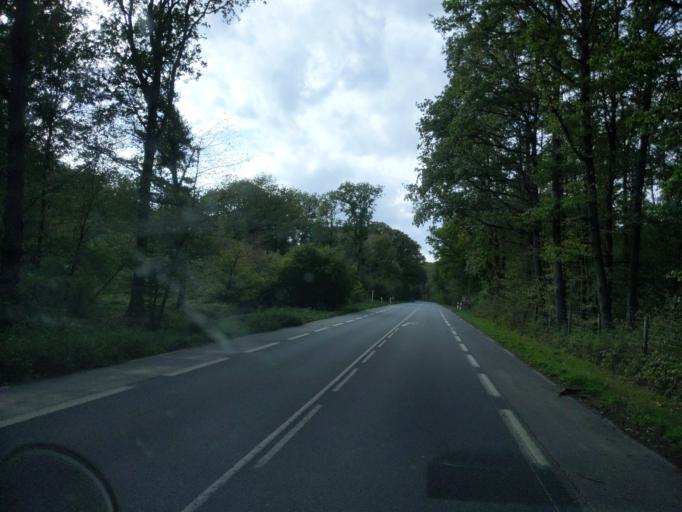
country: FR
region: Ile-de-France
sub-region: Departement des Yvelines
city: Auffargis
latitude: 48.6579
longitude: 1.9014
